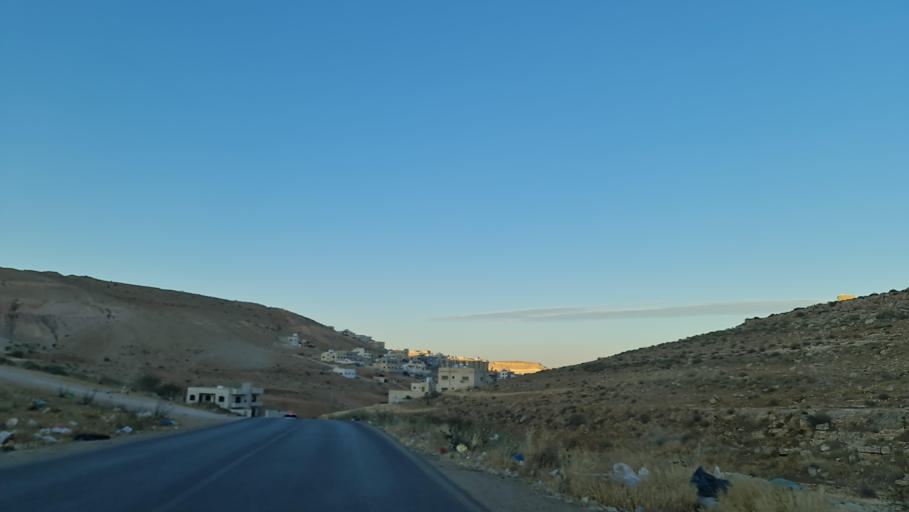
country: JO
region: Zarqa
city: Zarqa
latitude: 32.0823
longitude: 36.0452
